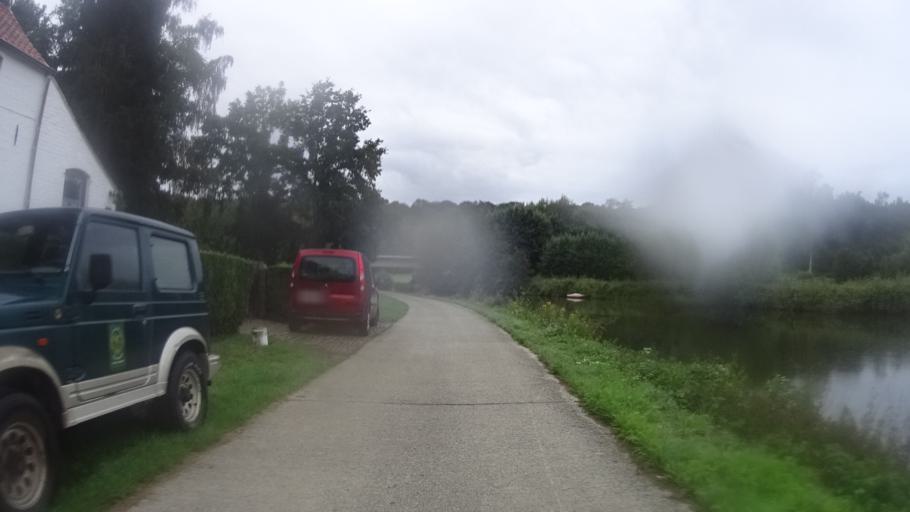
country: BE
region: Wallonia
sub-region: Province du Hainaut
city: Lobbes
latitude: 50.3480
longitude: 4.2559
